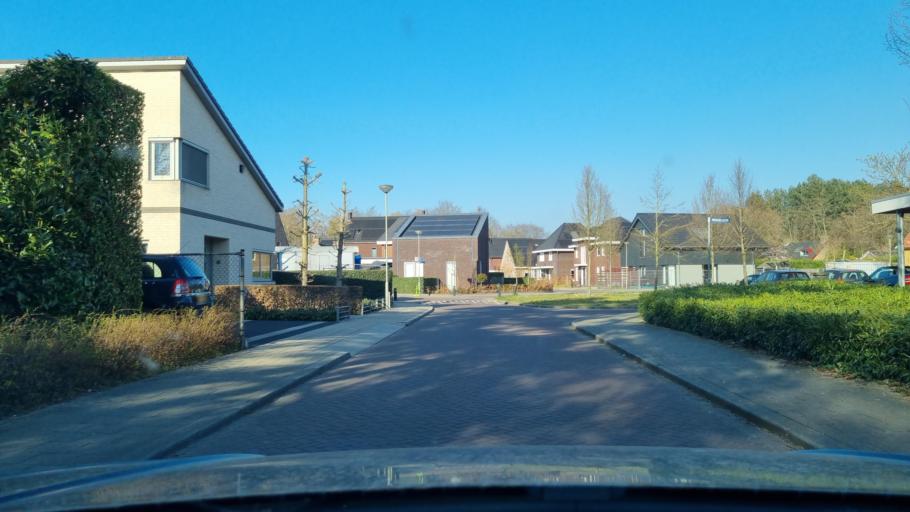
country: NL
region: Limburg
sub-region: Gemeente Gennep
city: Gennep
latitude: 51.7265
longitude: 5.9525
